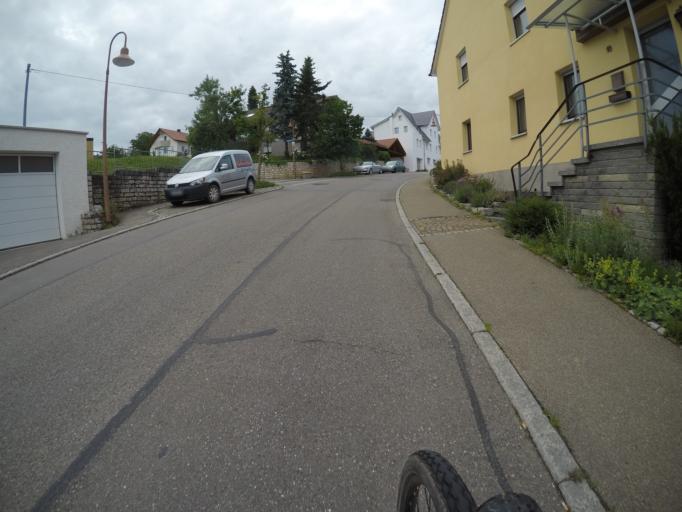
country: DE
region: Baden-Wuerttemberg
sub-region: Regierungsbezirk Stuttgart
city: Grossbettlingen
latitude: 48.5678
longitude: 9.3061
